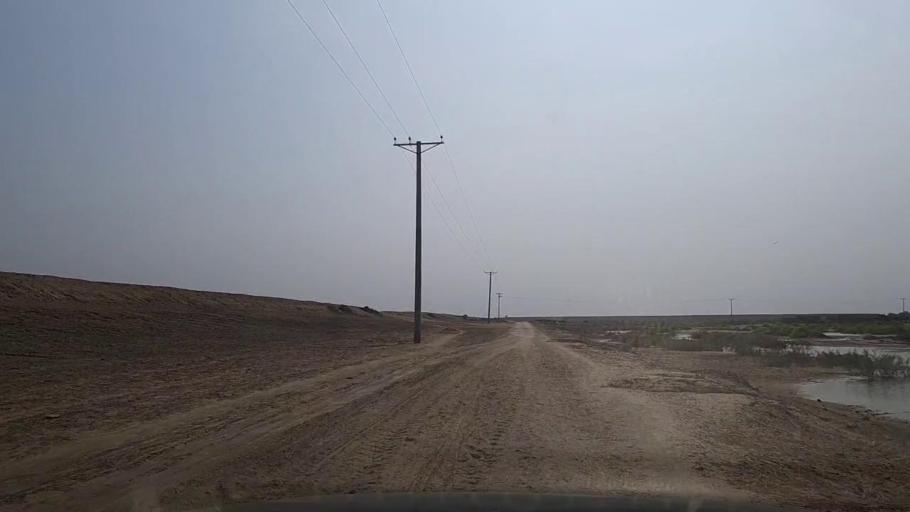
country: PK
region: Sindh
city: Thatta
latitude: 24.5764
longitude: 67.9158
